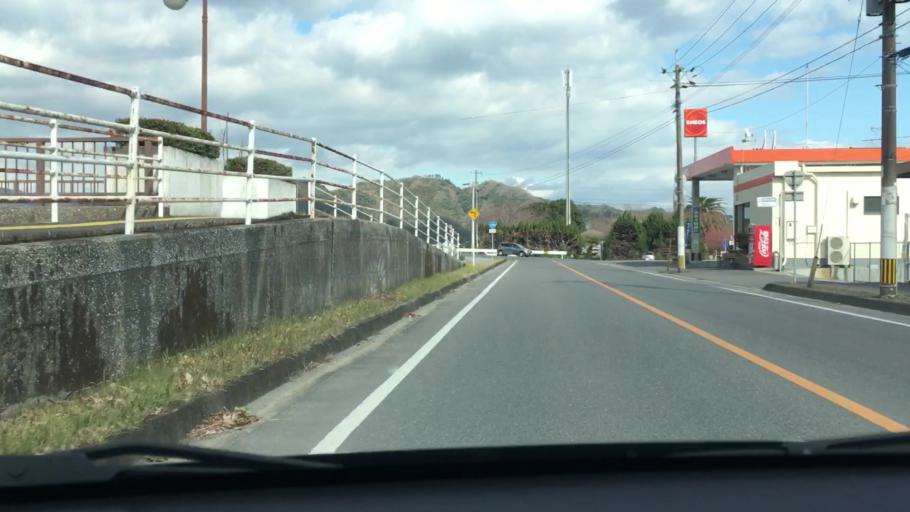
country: JP
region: Oita
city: Saiki
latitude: 32.9679
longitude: 131.9155
